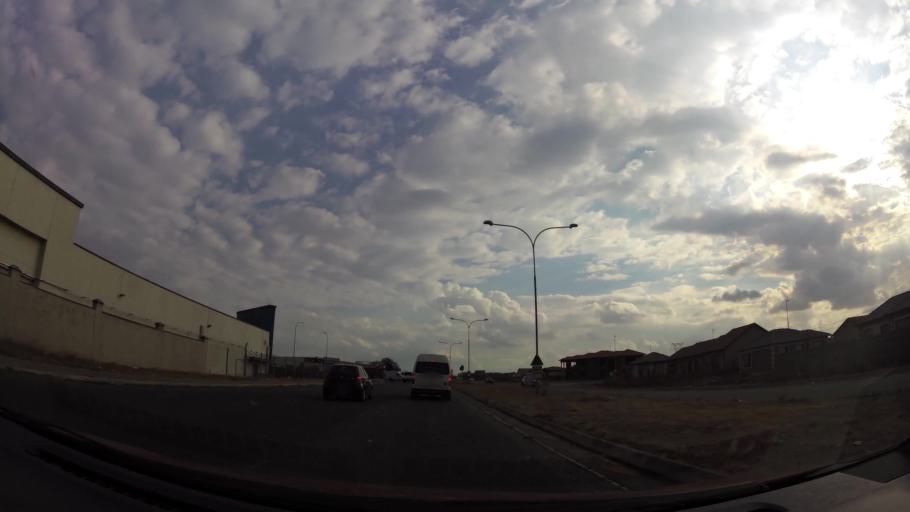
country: ZA
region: Gauteng
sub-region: Sedibeng District Municipality
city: Vereeniging
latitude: -26.6970
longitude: 27.8851
